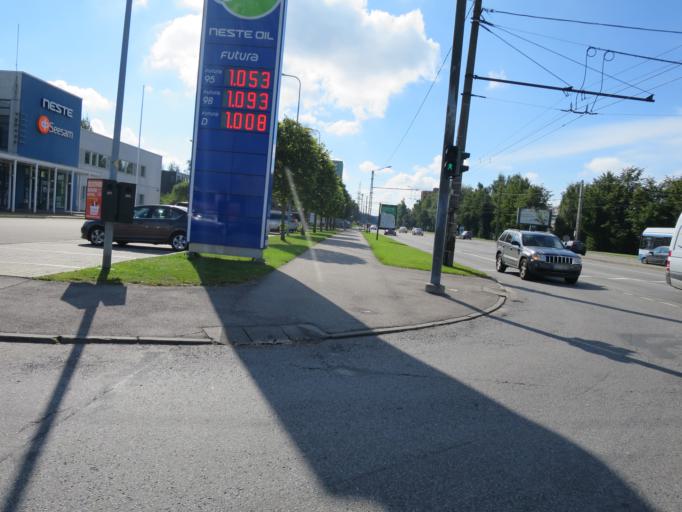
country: EE
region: Harju
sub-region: Tallinna linn
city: Tallinn
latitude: 59.4128
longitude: 24.7079
